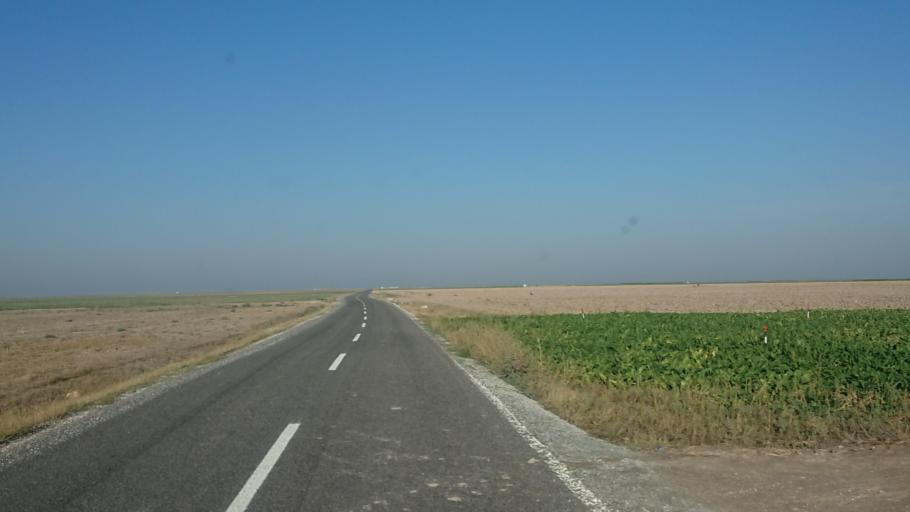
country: TR
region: Aksaray
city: Yesilova
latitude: 38.3877
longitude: 33.7877
